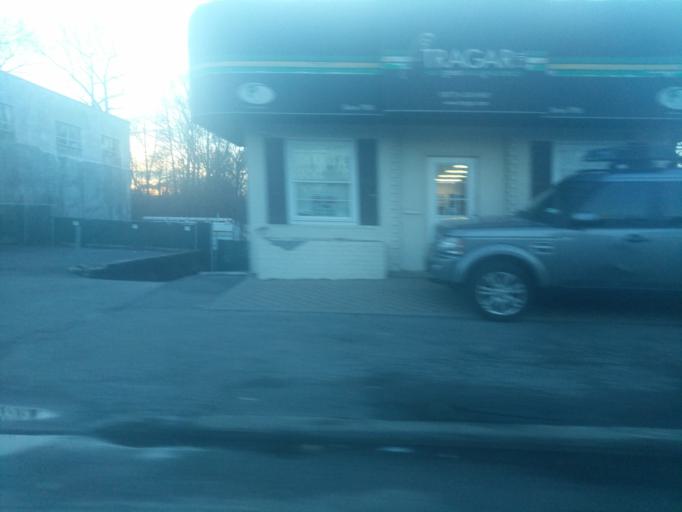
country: US
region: New York
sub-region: Nassau County
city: Wantagh
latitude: 40.6874
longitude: -73.5096
